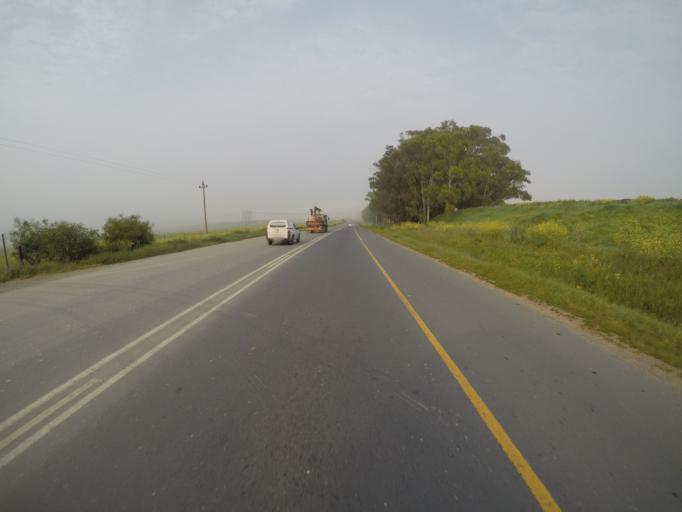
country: ZA
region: Western Cape
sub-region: City of Cape Town
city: Kraaifontein
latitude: -33.7959
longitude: 18.6926
